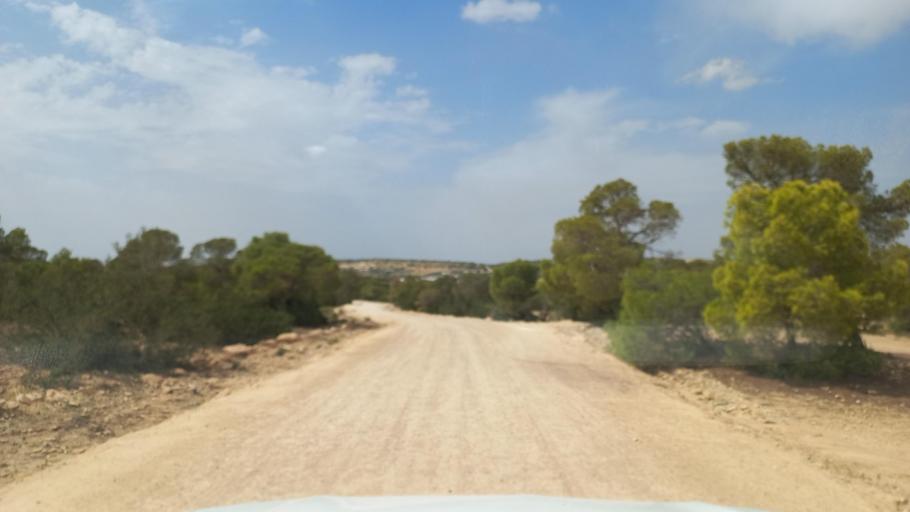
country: TN
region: Al Qasrayn
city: Kasserine
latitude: 35.3827
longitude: 8.8753
